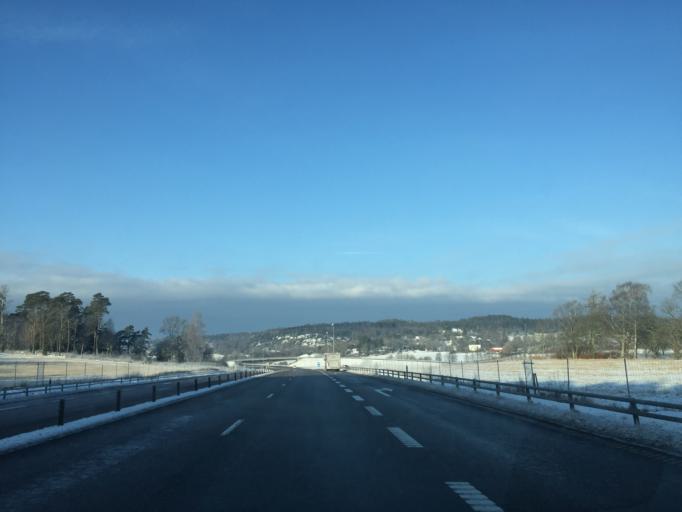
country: SE
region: Vaestra Goetaland
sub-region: Tanums Kommun
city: Tanumshede
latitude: 58.7317
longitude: 11.3329
